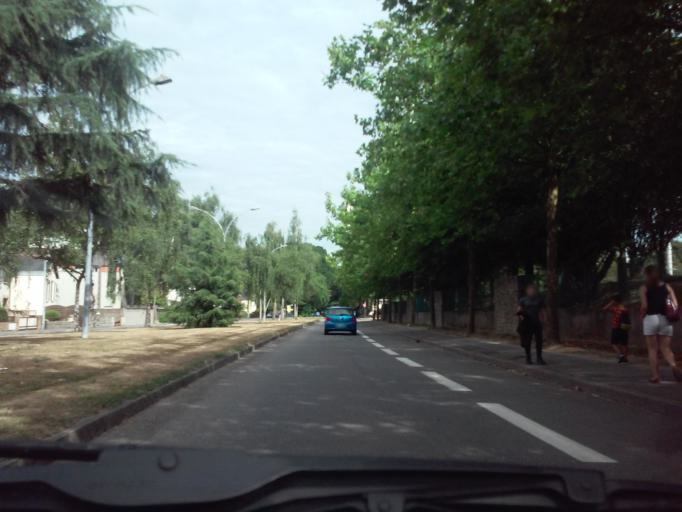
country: FR
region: Brittany
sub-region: Departement d'Ille-et-Vilaine
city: Rennes
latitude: 48.0899
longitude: -1.6869
